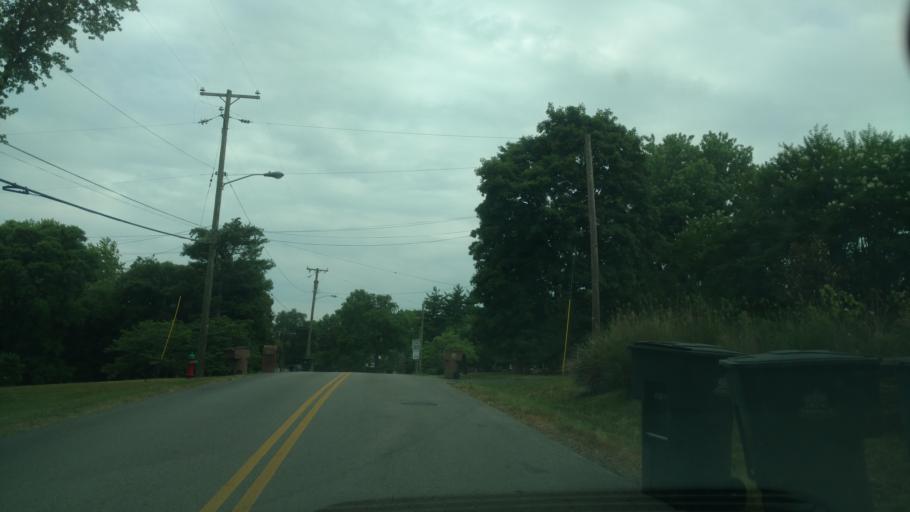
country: US
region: Tennessee
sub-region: Davidson County
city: Lakewood
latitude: 36.2143
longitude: -86.7071
